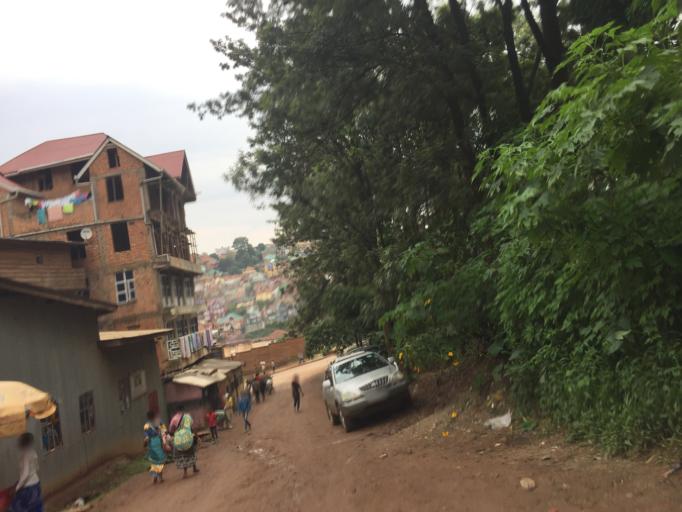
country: CD
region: South Kivu
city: Bukavu
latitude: -2.5028
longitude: 28.8504
